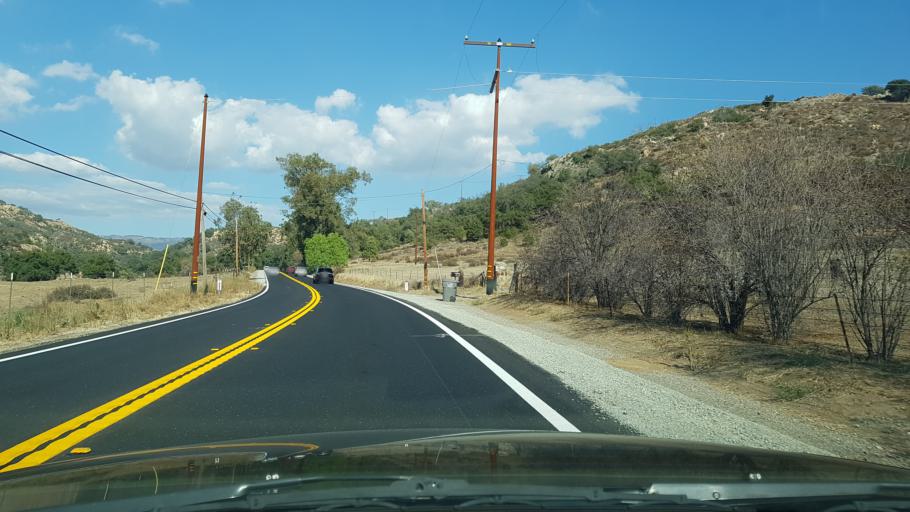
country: US
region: California
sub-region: San Diego County
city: San Diego Country Estates
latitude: 33.0832
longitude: -116.7119
